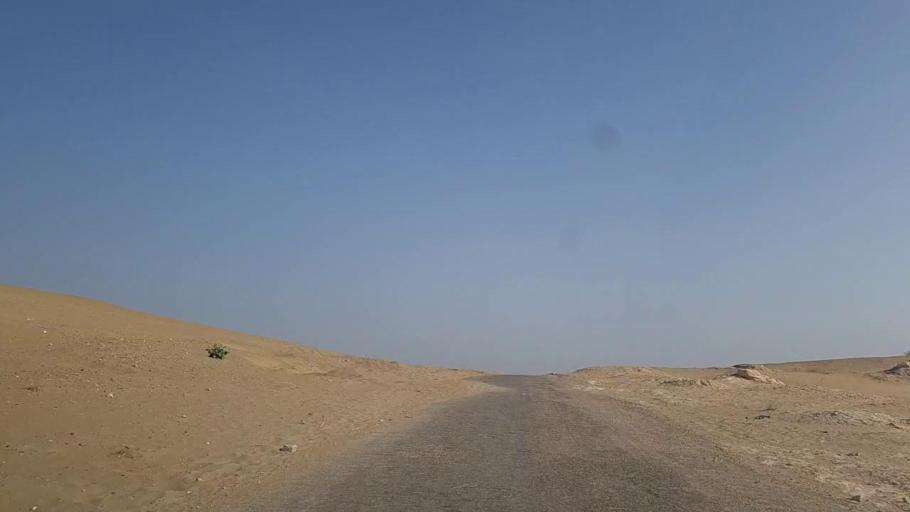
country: PK
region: Sindh
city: Naukot
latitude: 24.6287
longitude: 69.3637
